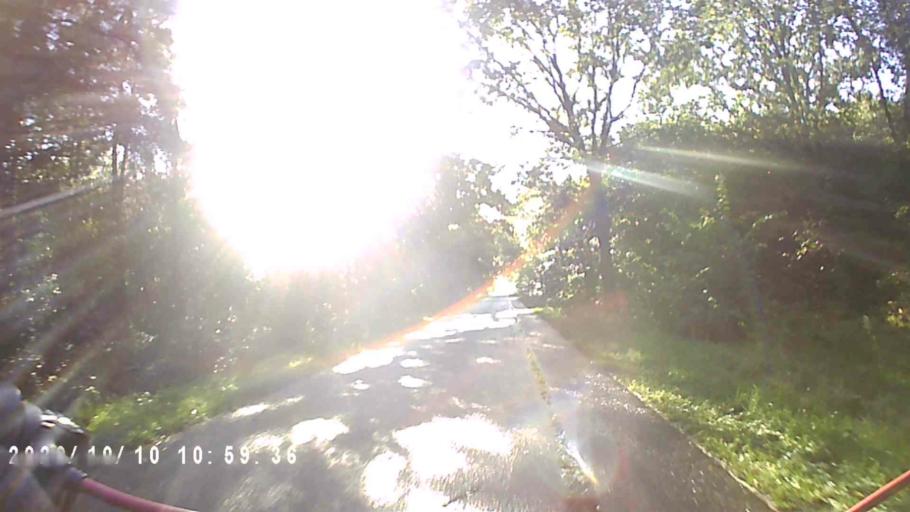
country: NL
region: Friesland
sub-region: Gemeente Achtkarspelen
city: Surhuisterveen
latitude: 53.1416
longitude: 6.2099
